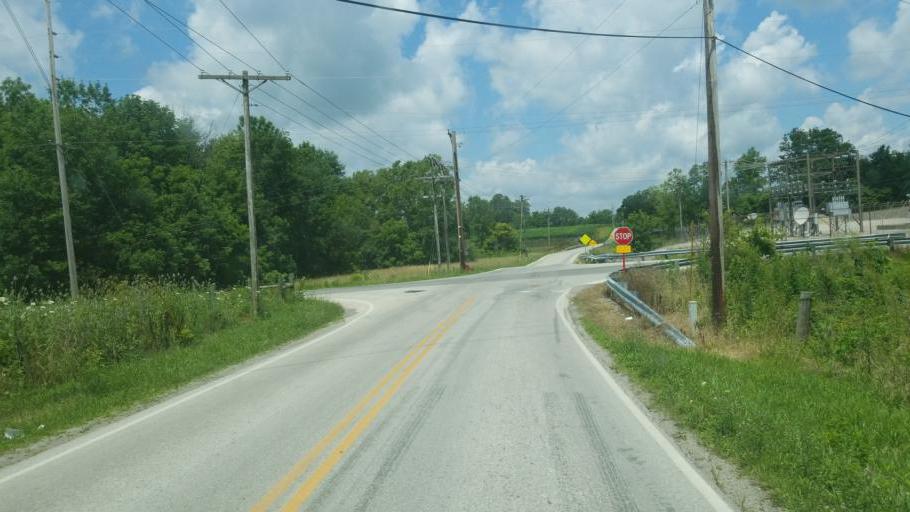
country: US
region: Ohio
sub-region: Highland County
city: Leesburg
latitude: 39.2523
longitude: -83.4722
